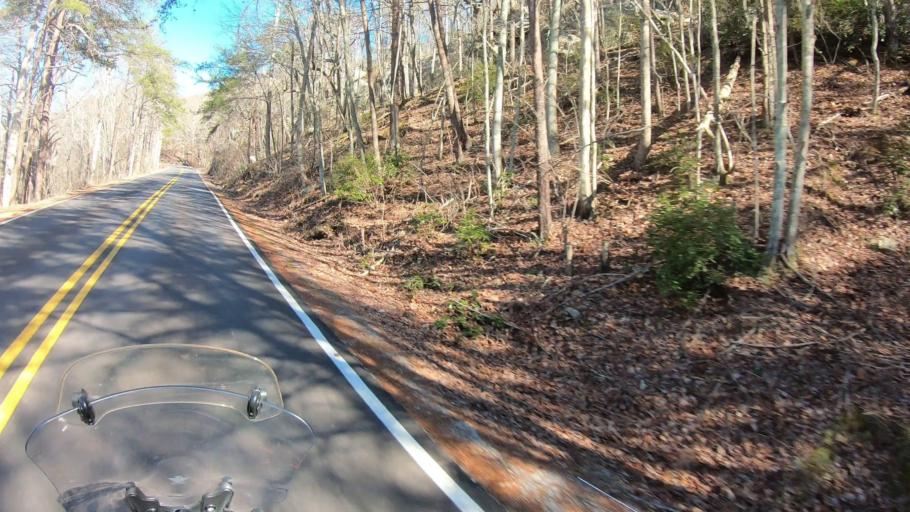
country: US
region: Alabama
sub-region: Talladega County
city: Munford
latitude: 33.4636
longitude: -85.8149
